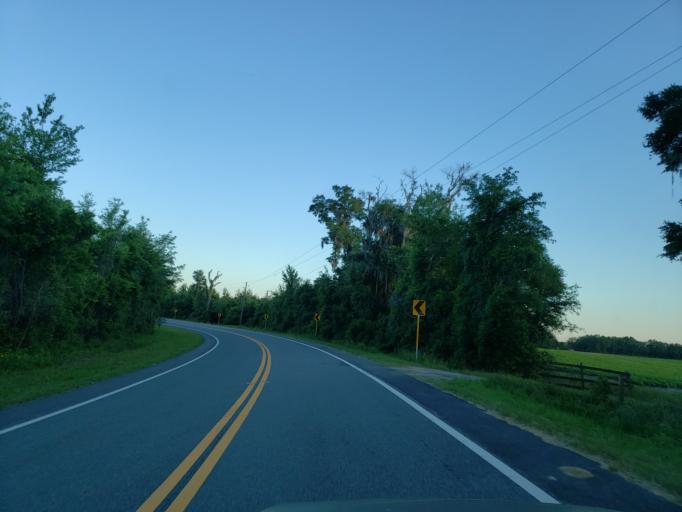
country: US
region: Florida
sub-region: Madison County
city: Madison
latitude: 30.5834
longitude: -83.2413
